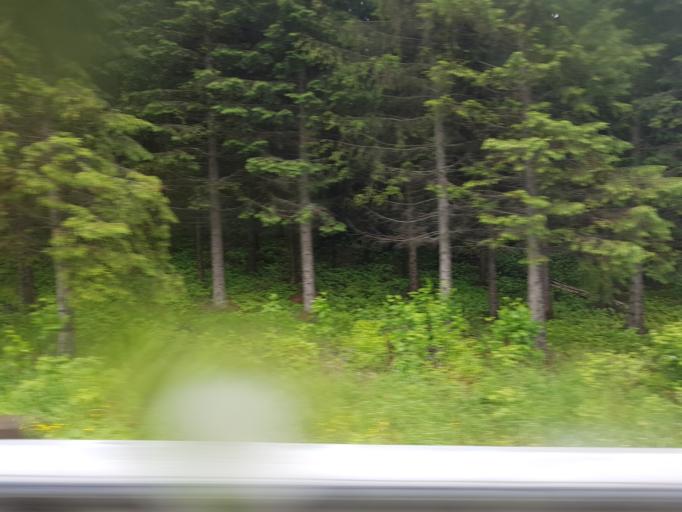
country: NO
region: Nord-Trondelag
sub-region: Stjordal
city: Stjordalshalsen
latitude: 63.4008
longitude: 10.9471
